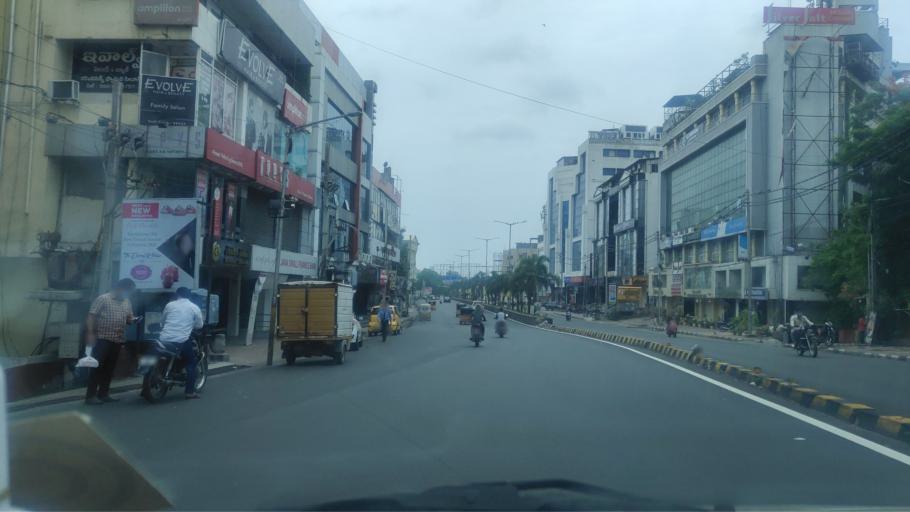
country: IN
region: Telangana
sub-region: Hyderabad
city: Hyderabad
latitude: 17.4105
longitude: 78.4498
